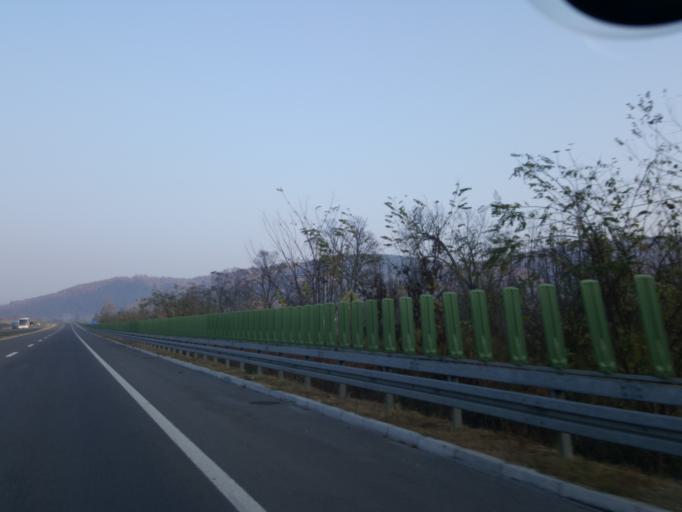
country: RS
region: Central Serbia
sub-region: Jablanicki Okrug
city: Vlasotince
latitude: 42.9035
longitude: 22.0502
